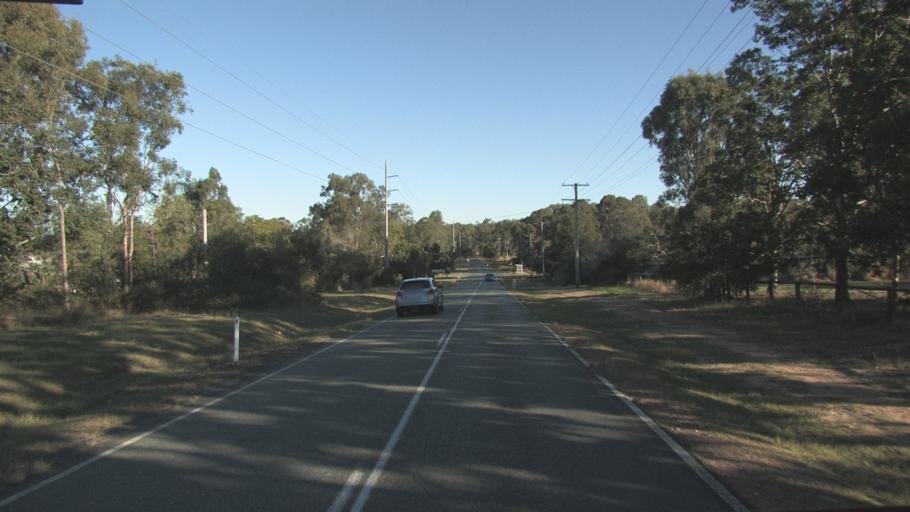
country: AU
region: Queensland
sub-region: Logan
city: Logan Reserve
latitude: -27.7370
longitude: 153.0876
